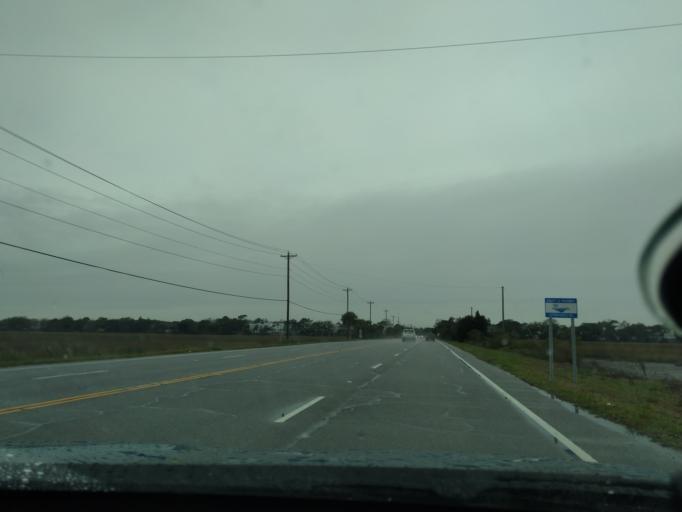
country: US
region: South Carolina
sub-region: Charleston County
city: Folly Beach
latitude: 32.6808
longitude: -79.9557
